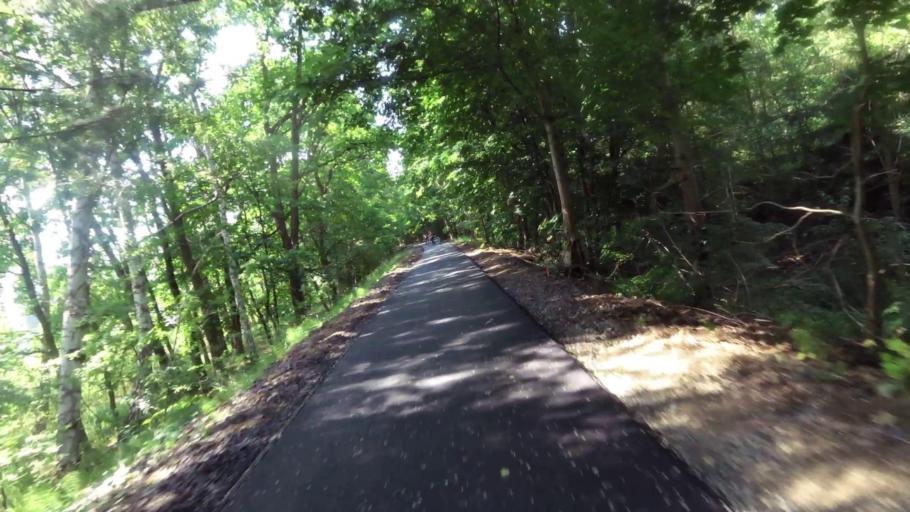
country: PL
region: West Pomeranian Voivodeship
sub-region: Powiat gryfinski
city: Gryfino
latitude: 53.2207
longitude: 14.5936
